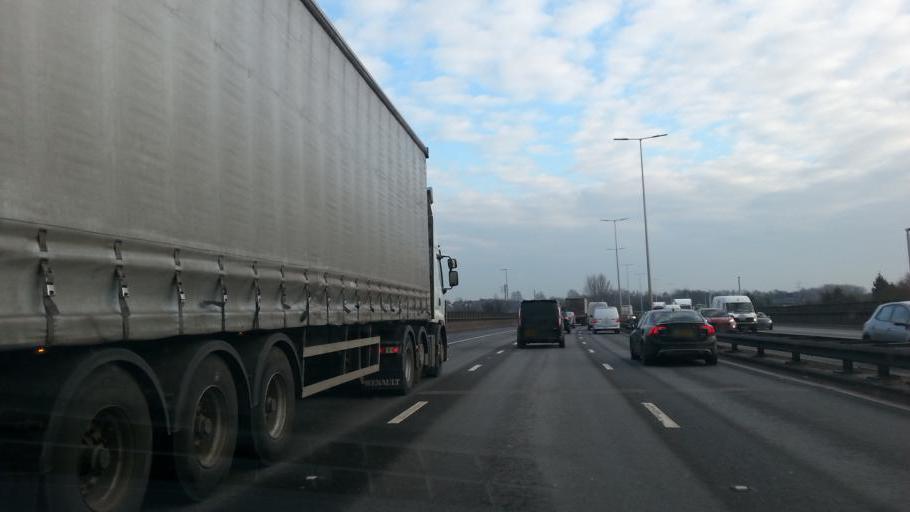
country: GB
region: England
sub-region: City and Borough of Birmingham
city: Hockley
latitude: 52.5375
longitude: -1.9059
